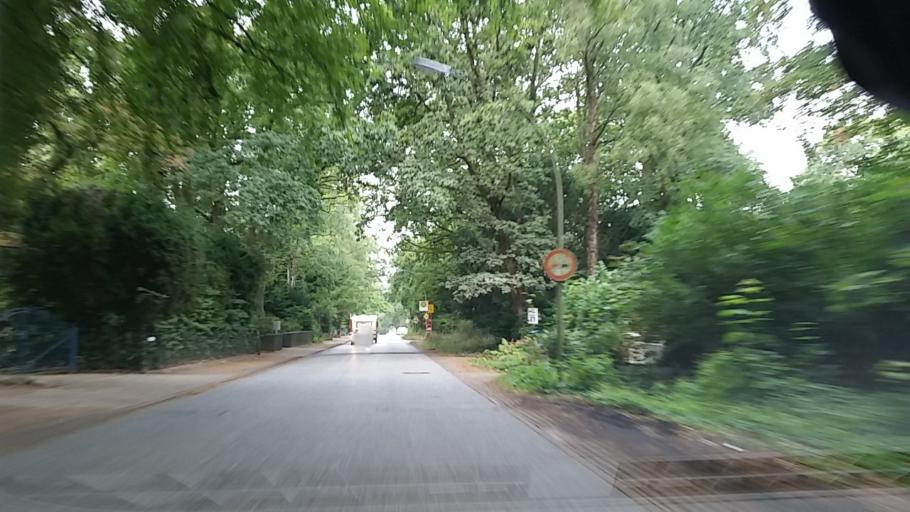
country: DE
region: Schleswig-Holstein
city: Wedel
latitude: 53.5714
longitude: 9.7525
